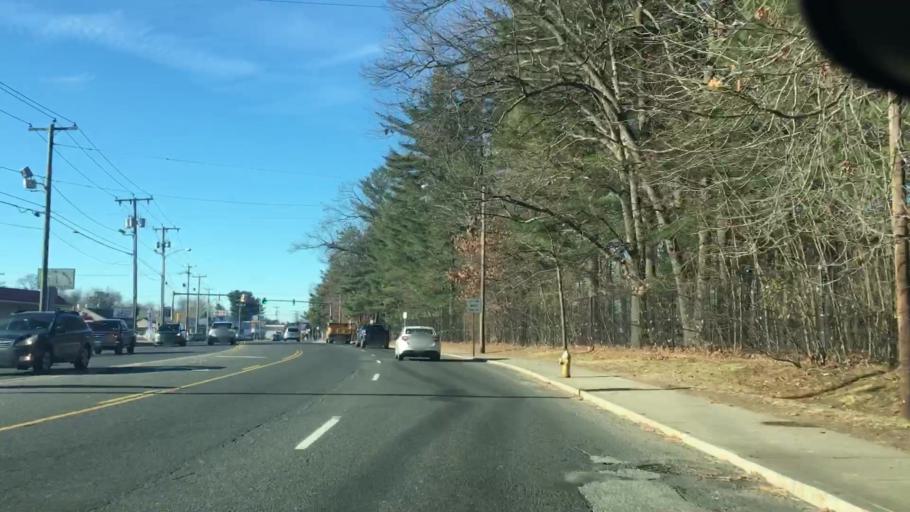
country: US
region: Massachusetts
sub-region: Hampden County
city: Ludlow
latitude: 42.1389
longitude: -72.5106
